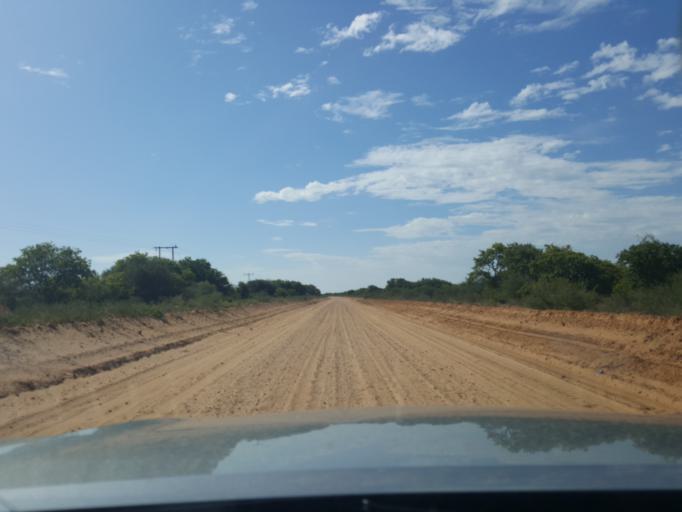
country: BW
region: Kweneng
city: Khudumelapye
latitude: -23.7477
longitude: 24.7535
